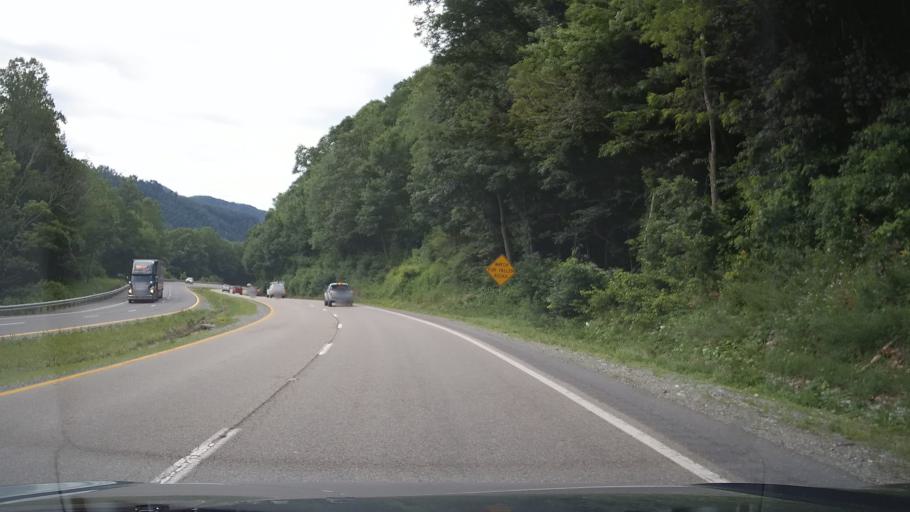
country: US
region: Virginia
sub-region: Wise County
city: Wise
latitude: 37.0210
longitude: -82.5887
